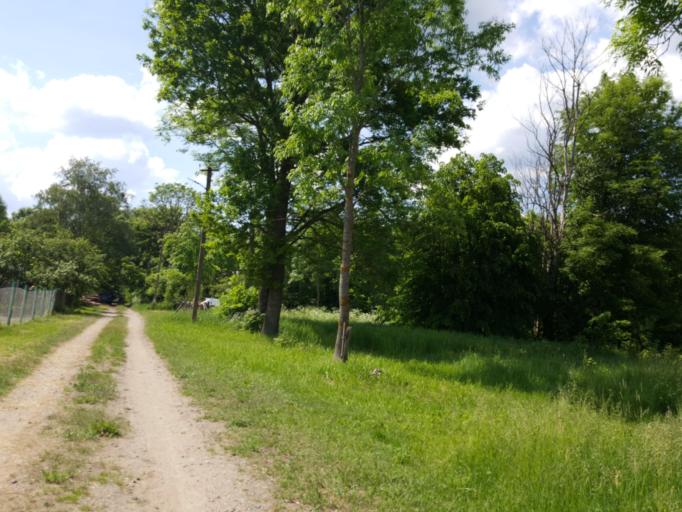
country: PL
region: Podlasie
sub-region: Powiat hajnowski
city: Hajnowka
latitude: 52.5665
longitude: 23.6074
